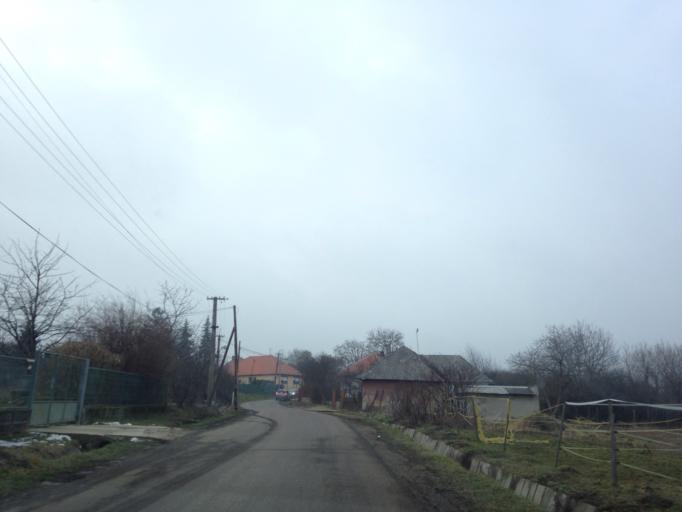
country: SK
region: Nitriansky
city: Svodin
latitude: 47.9870
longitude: 18.3974
